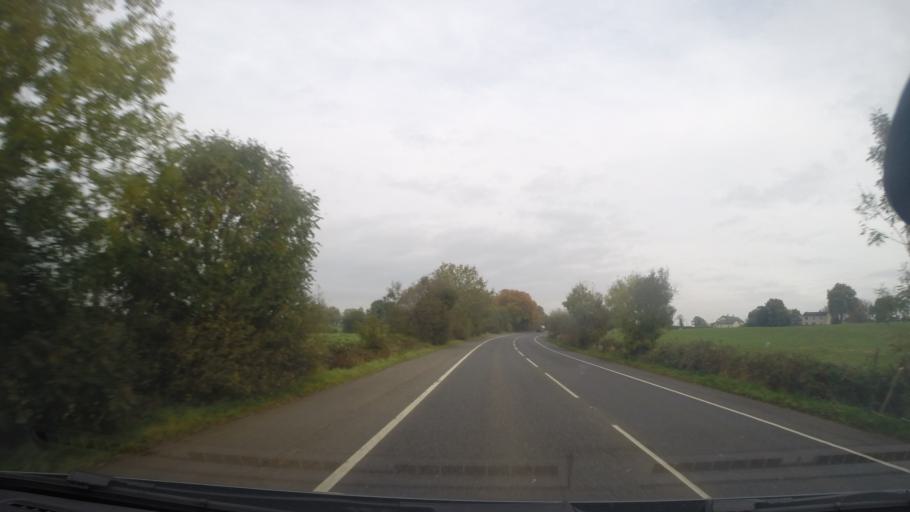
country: GB
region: Northern Ireland
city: Fivemiletown
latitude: 54.3320
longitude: -7.3867
